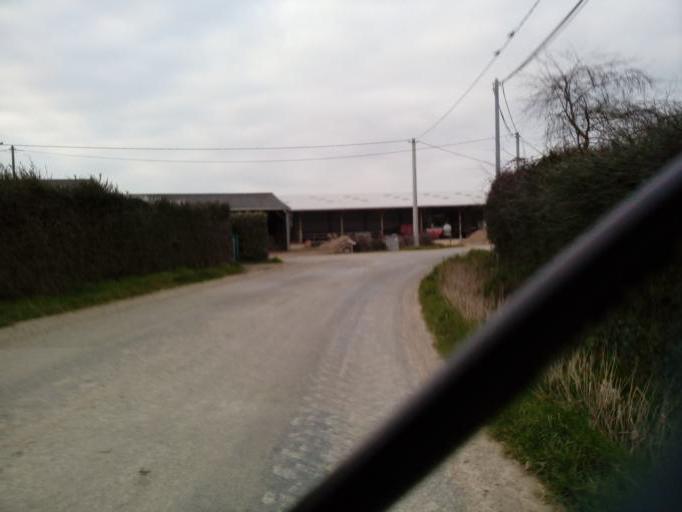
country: FR
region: Brittany
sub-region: Departement d'Ille-et-Vilaine
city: Cintre
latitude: 48.1035
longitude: -1.8950
